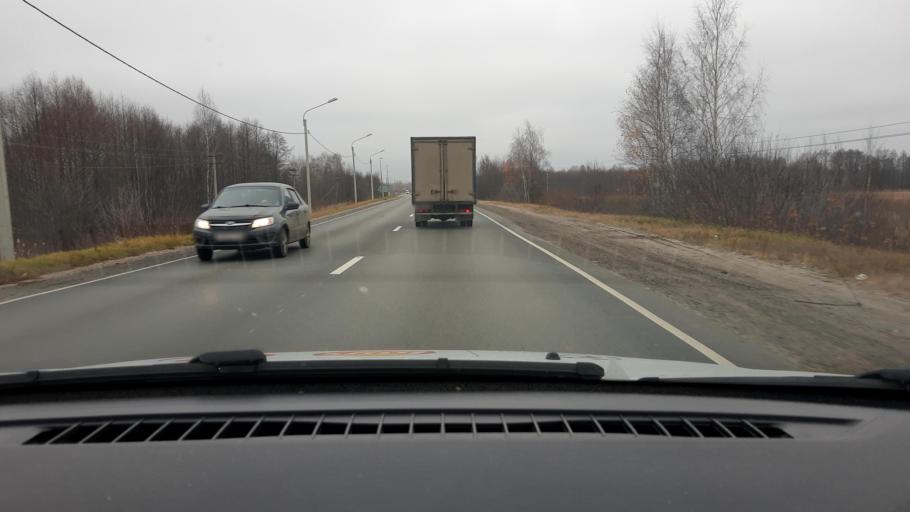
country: RU
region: Nizjnij Novgorod
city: Gorodets
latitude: 56.6097
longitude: 43.4440
